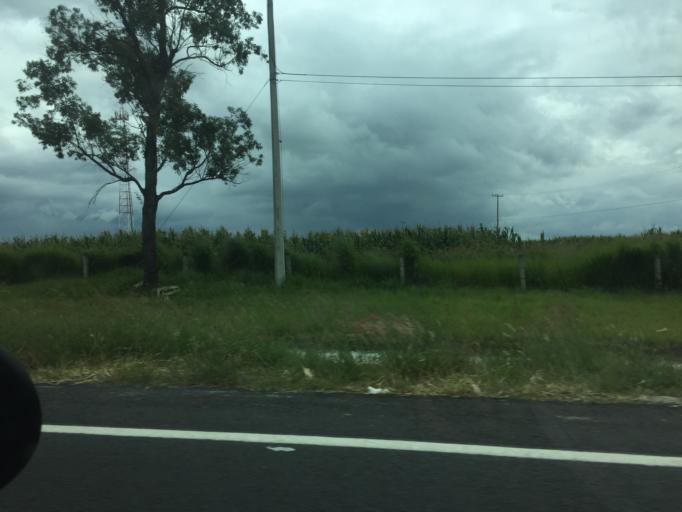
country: MX
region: Jalisco
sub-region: Tonala
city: Mismaloya (Fraccionamiento Pedregal de Santa Martha)
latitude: 20.6059
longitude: -103.1323
